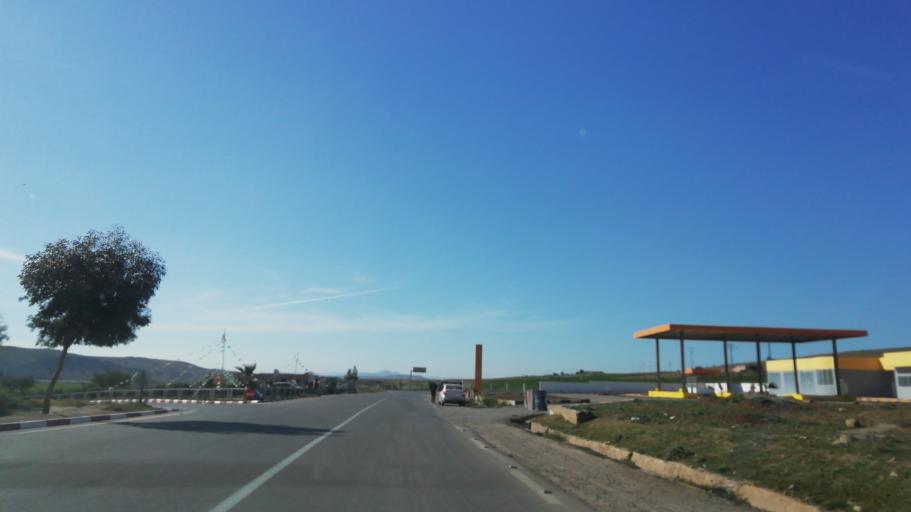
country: DZ
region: Mascara
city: Oued el Abtal
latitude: 35.4509
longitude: 0.7817
